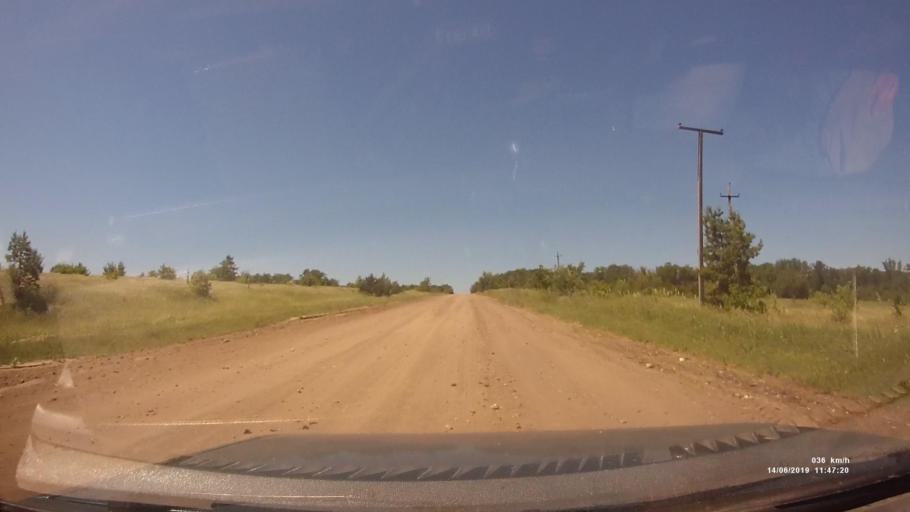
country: RU
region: Rostov
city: Kazanskaya
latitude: 49.8511
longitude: 41.2969
